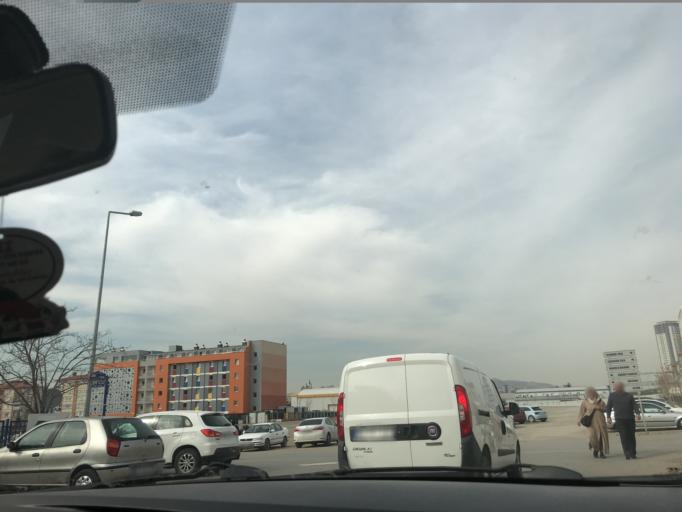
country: TR
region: Ankara
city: Batikent
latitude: 39.9629
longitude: 32.7674
